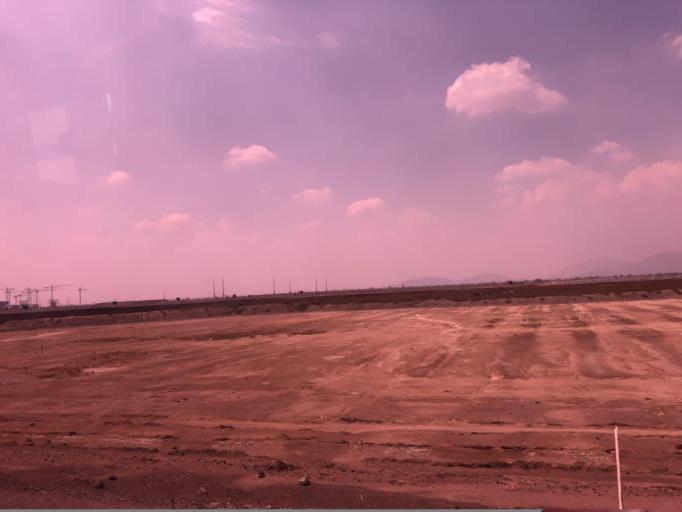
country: MX
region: Mexico
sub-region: Texcoco
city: Colonia Lazaro Cardenas
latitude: 19.5164
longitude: -98.9859
